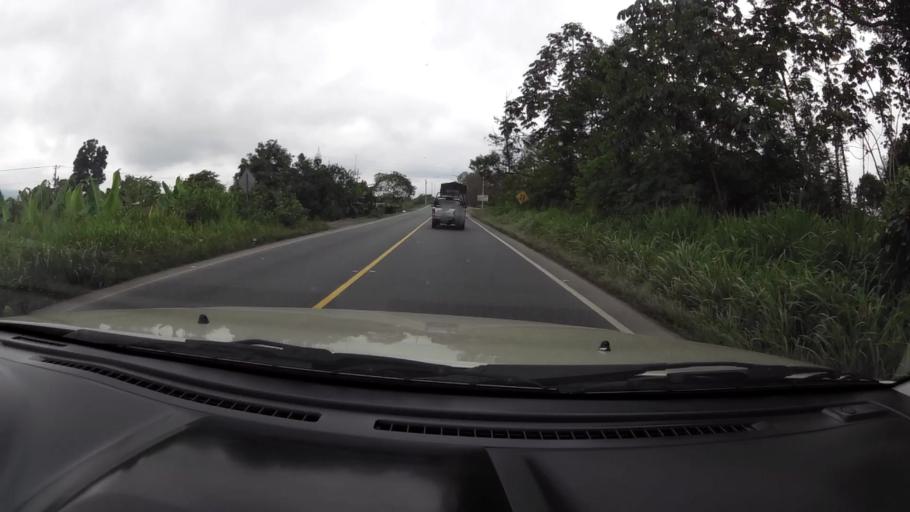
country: EC
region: Guayas
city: Balao
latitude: -2.8146
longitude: -79.7113
